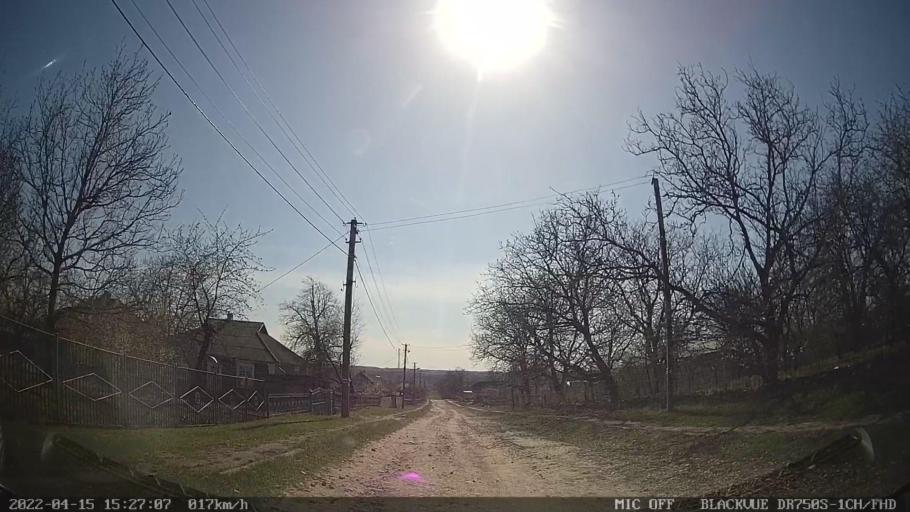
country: MD
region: Raionul Ocnita
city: Otaci
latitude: 48.3606
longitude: 27.9276
